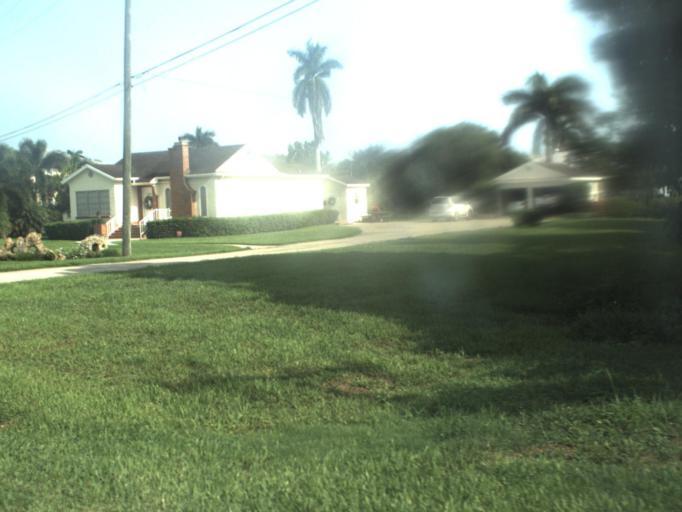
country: US
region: Florida
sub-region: Palm Beach County
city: Belle Glade
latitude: 26.6945
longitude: -80.6844
